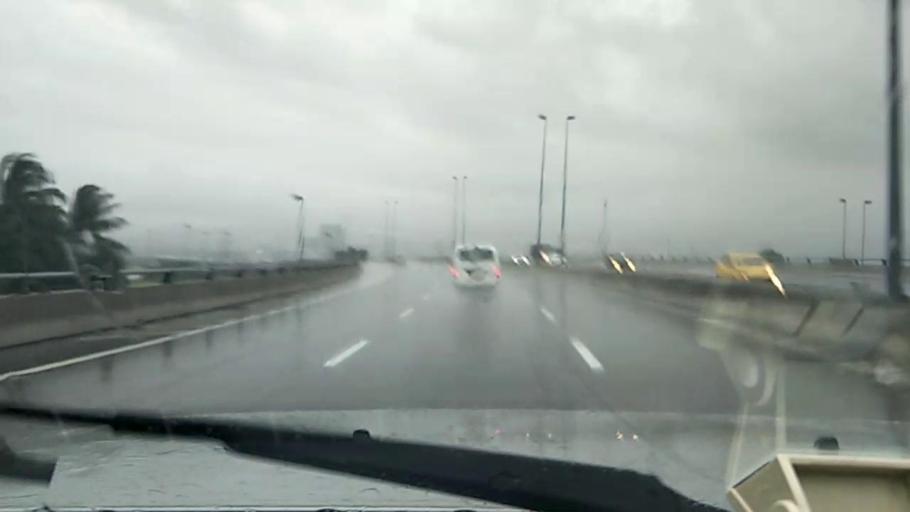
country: MY
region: Selangor
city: Kampong Baharu Balakong
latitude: 2.9918
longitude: 101.7723
